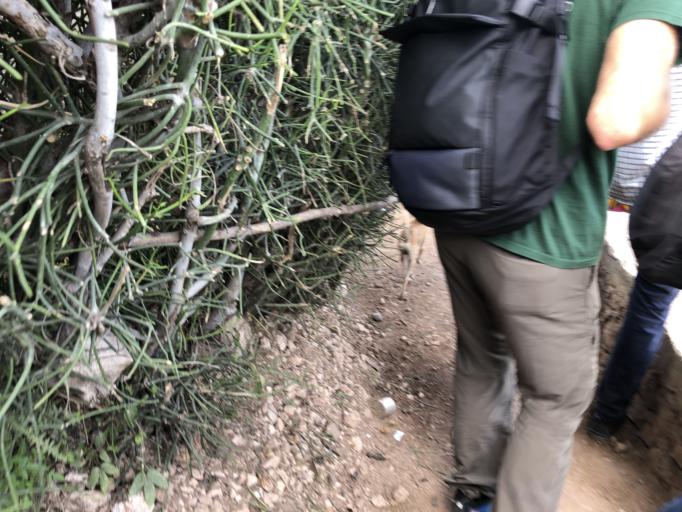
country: HT
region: Ouest
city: Port-au-Prince
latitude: 18.5210
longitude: -72.3177
